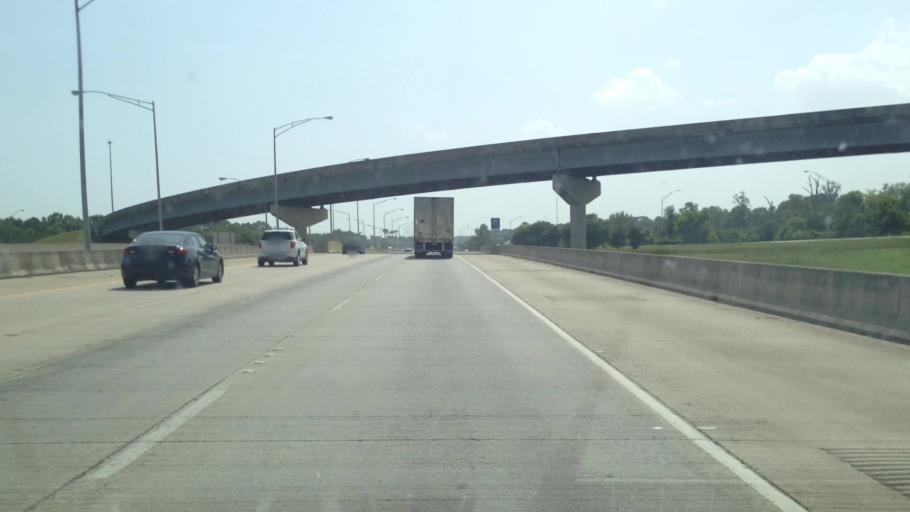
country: US
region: Louisiana
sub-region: Caddo Parish
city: Shreveport
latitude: 32.4558
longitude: -93.8461
